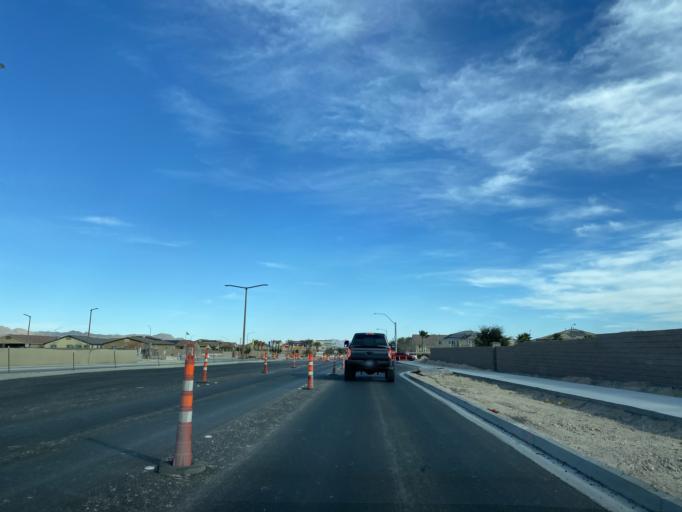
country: US
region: Nevada
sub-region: Clark County
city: North Las Vegas
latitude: 36.2912
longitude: -115.1996
